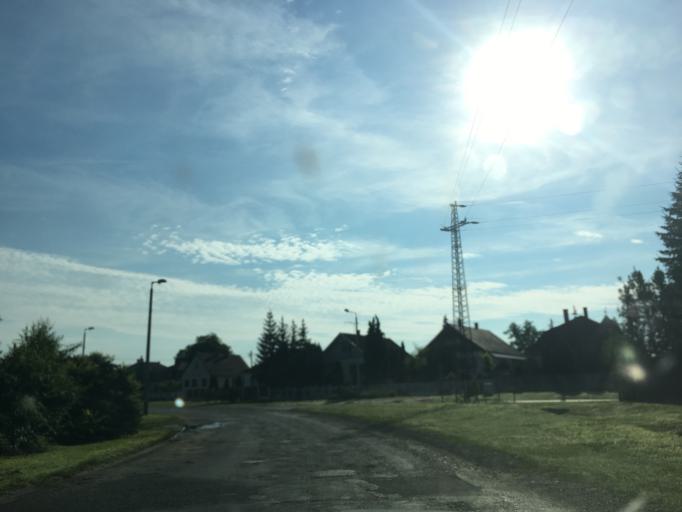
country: HU
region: Szabolcs-Szatmar-Bereg
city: Nyirlugos
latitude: 47.6911
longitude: 22.0362
